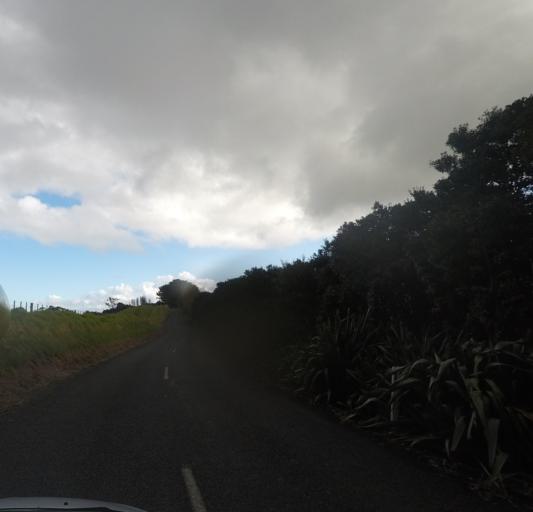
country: NZ
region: Auckland
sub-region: Auckland
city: Warkworth
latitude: -36.3722
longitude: 174.7644
